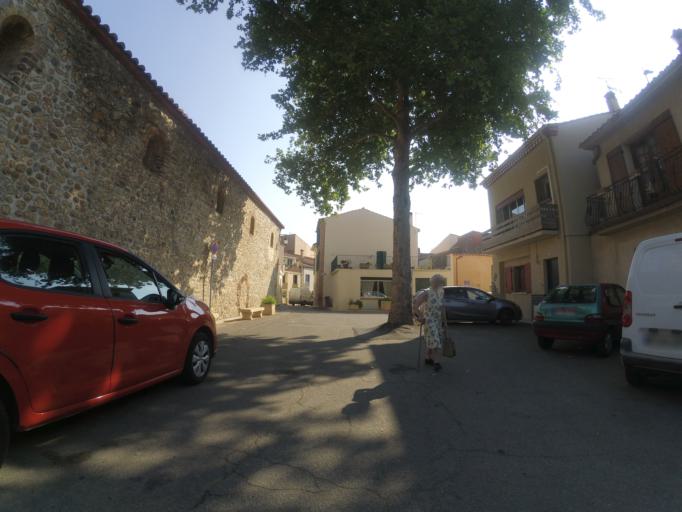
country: FR
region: Languedoc-Roussillon
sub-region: Departement des Pyrenees-Orientales
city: Saint-Esteve
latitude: 42.7080
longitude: 2.8452
